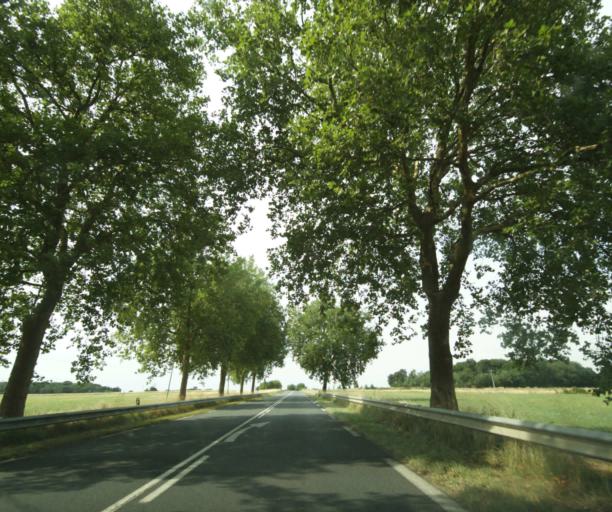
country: FR
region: Centre
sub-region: Departement d'Indre-et-Loire
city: Saint-Christophe-sur-le-Nais
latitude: 47.6322
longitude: 0.5025
